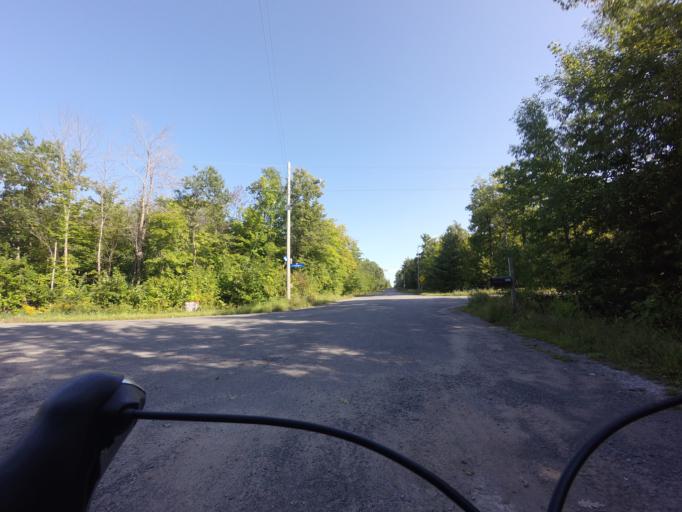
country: CA
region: Ontario
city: Bells Corners
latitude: 45.4850
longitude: -76.0498
